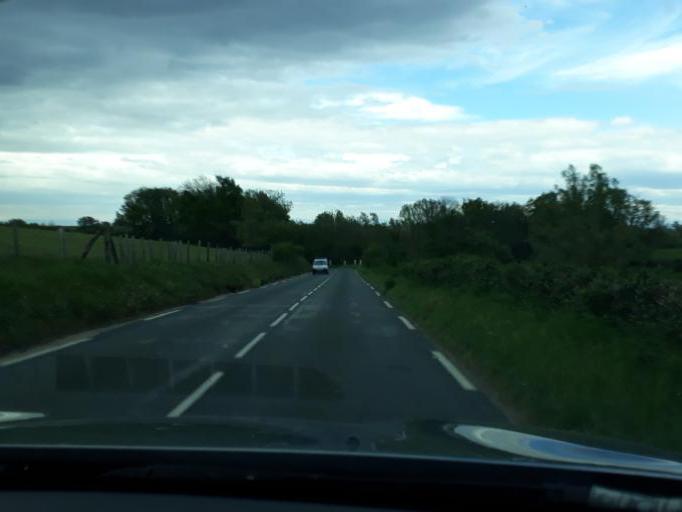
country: FR
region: Rhone-Alpes
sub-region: Departement du Rhone
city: Soucieu-en-Jarrest
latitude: 45.6775
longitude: 4.7206
